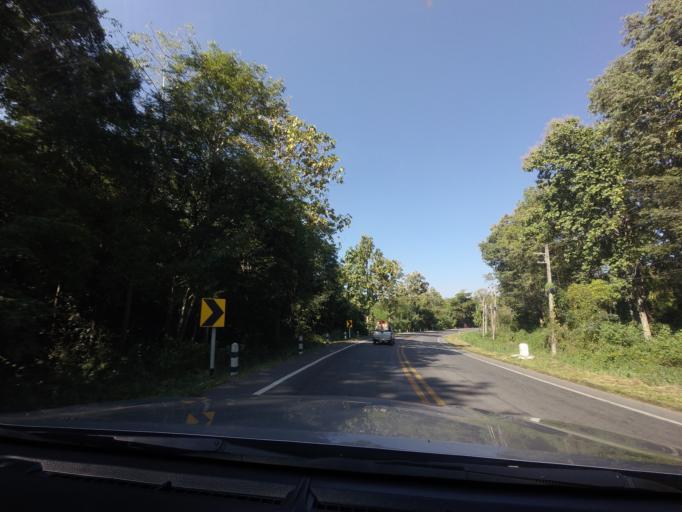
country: TH
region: Sukhothai
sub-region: Amphoe Si Satchanalai
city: Si Satchanalai
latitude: 17.6102
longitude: 99.7066
